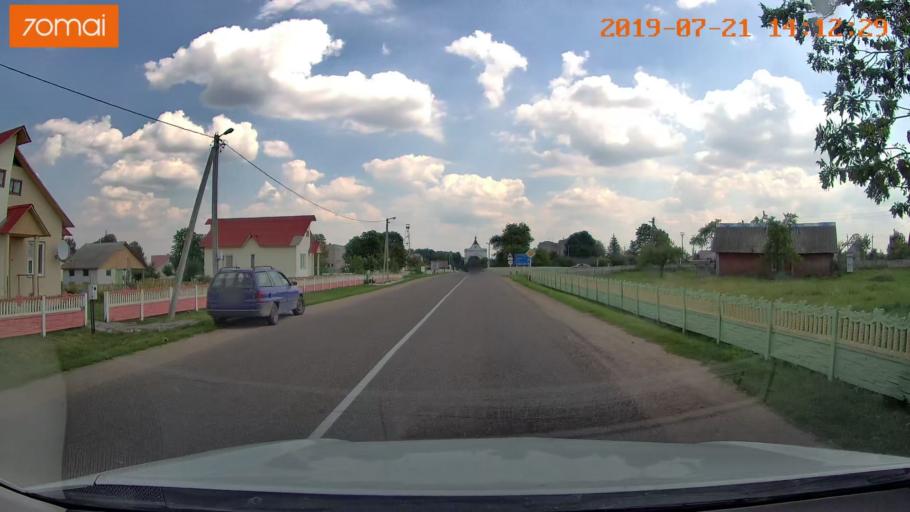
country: BY
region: Grodnenskaya
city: Karelichy
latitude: 53.6523
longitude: 26.1685
